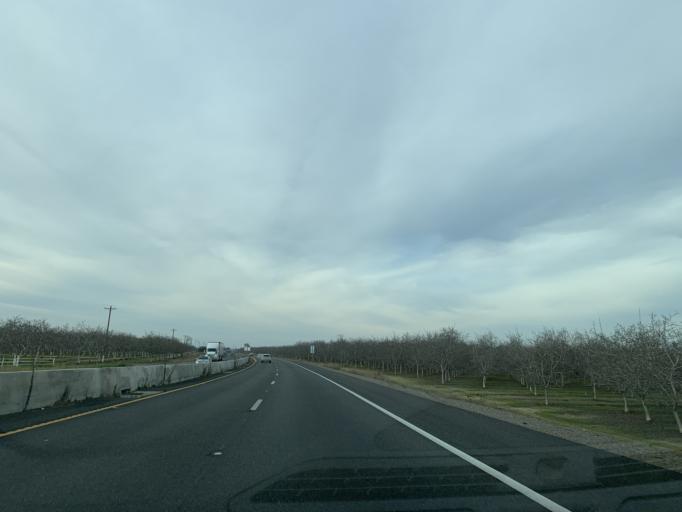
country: US
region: California
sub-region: Yuba County
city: Plumas Lake
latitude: 38.9083
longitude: -121.5938
